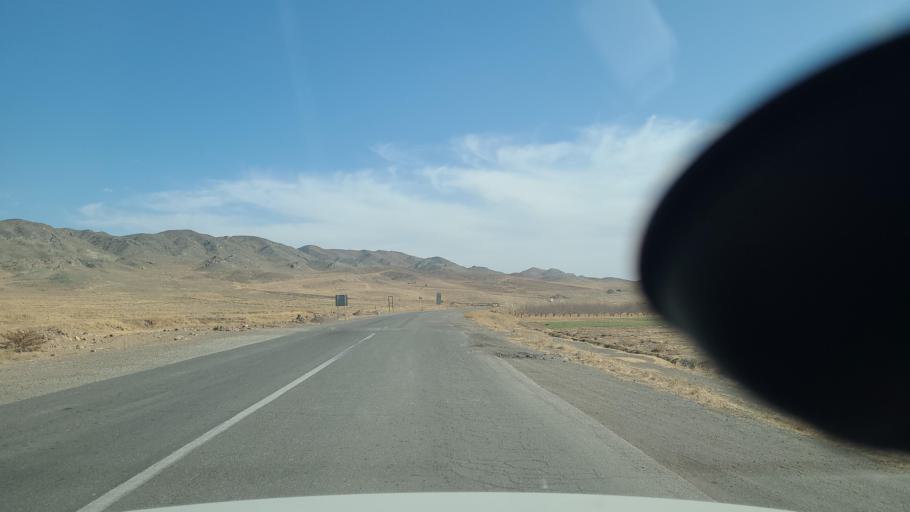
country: IR
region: Razavi Khorasan
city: Fariman
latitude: 35.5979
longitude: 59.7009
